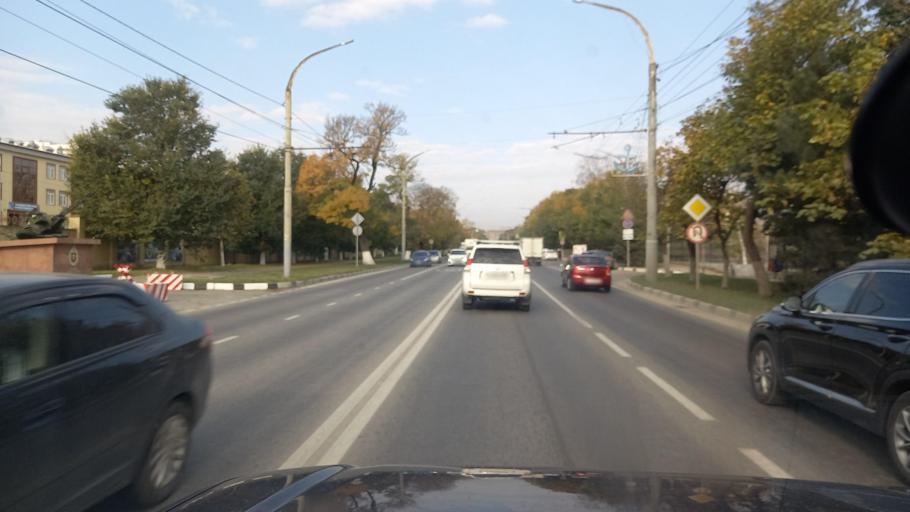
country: RU
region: Krasnodarskiy
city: Novorossiysk
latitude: 44.7383
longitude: 37.7375
